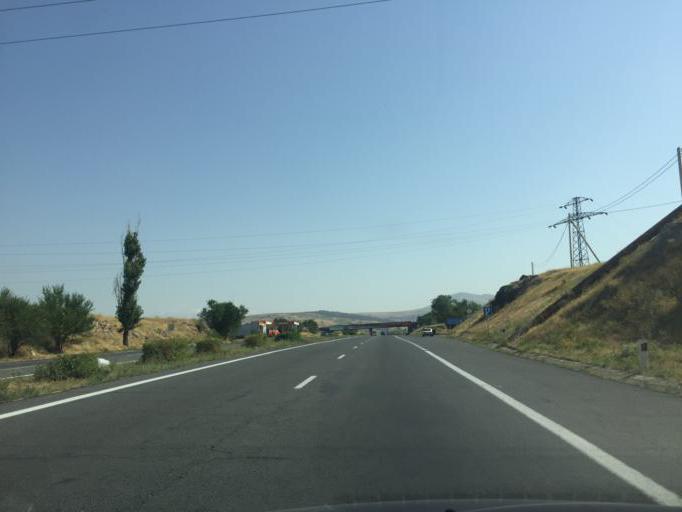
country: AM
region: Kotayk'i Marz
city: Arzni
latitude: 40.2824
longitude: 44.6044
